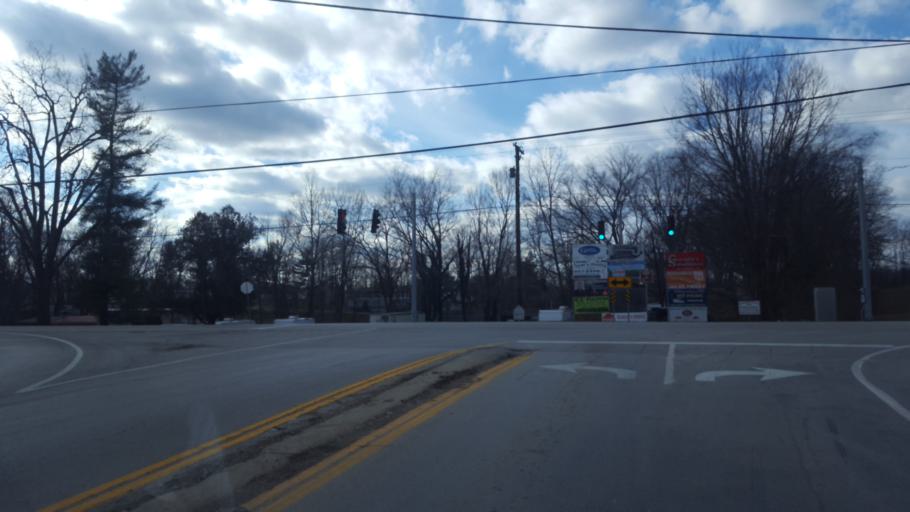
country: US
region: Kentucky
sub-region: Scott County
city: Georgetown
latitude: 38.2784
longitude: -84.5678
